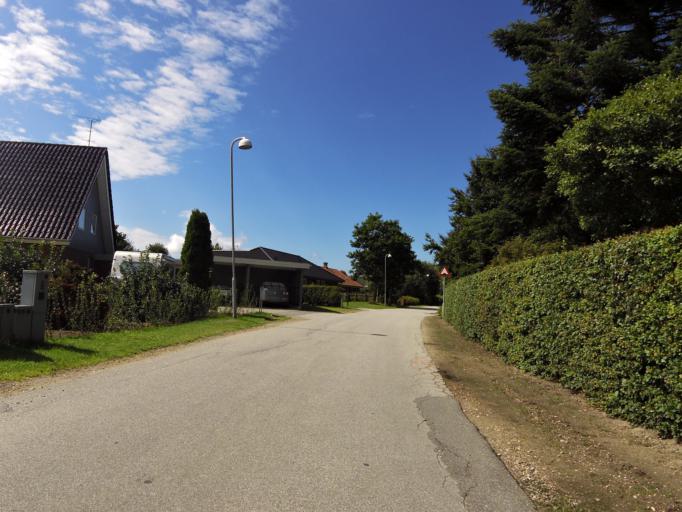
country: DK
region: South Denmark
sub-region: Esbjerg Kommune
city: Ribe
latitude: 55.3100
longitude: 8.7729
